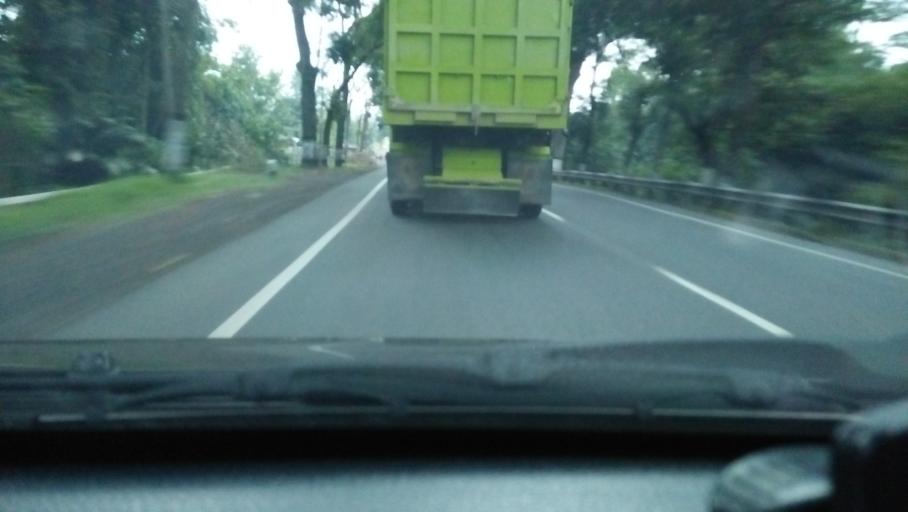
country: ID
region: Central Java
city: Magelang
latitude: -7.3881
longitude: 110.2500
